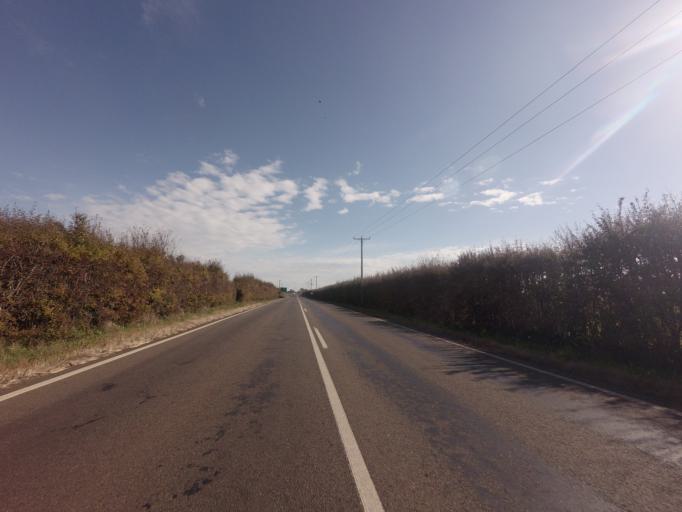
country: AU
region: Tasmania
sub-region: Meander Valley
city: Westbury
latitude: -41.5261
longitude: 146.8794
